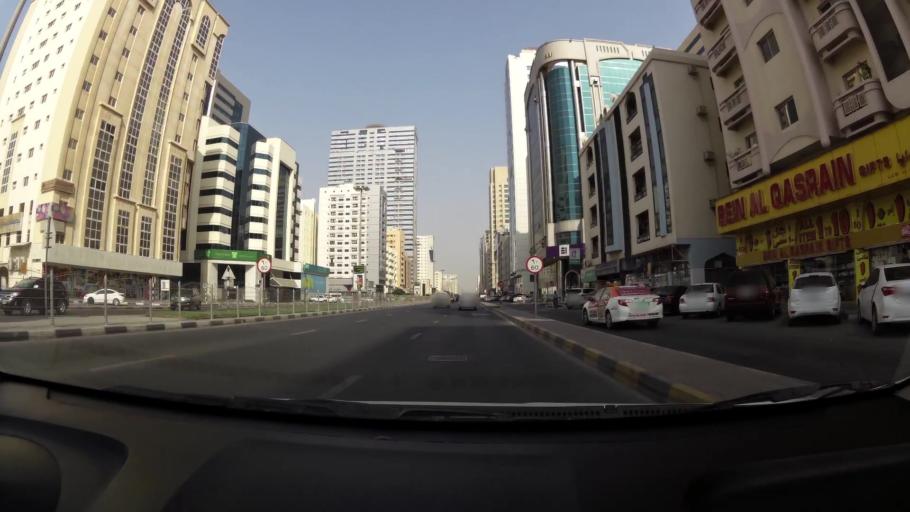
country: AE
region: Ash Shariqah
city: Sharjah
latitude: 25.3473
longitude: 55.3892
